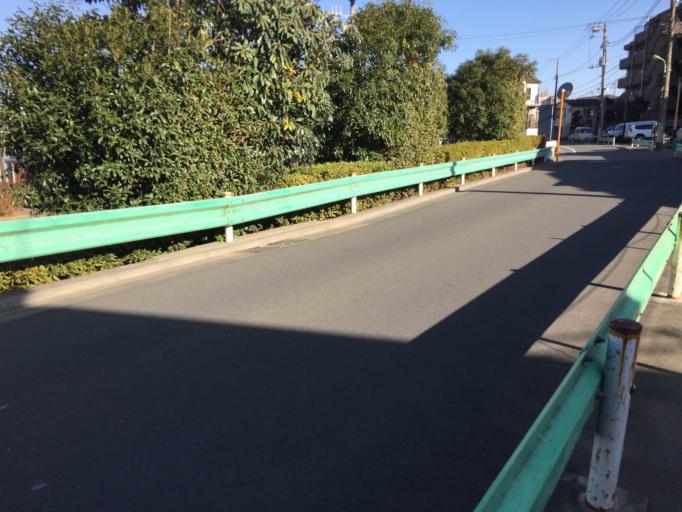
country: JP
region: Tokyo
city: Chofugaoka
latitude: 35.6171
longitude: 139.6145
